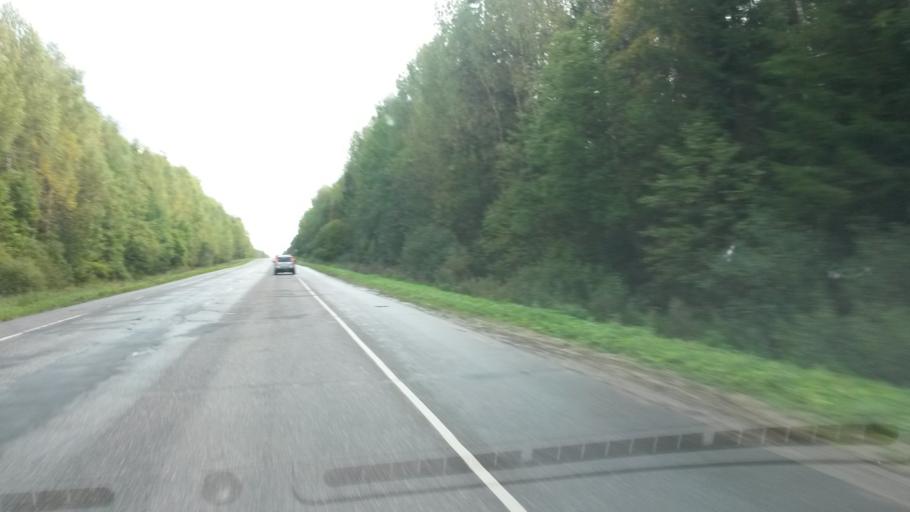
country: RU
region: Ivanovo
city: Kaminskiy
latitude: 57.0752
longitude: 41.4602
